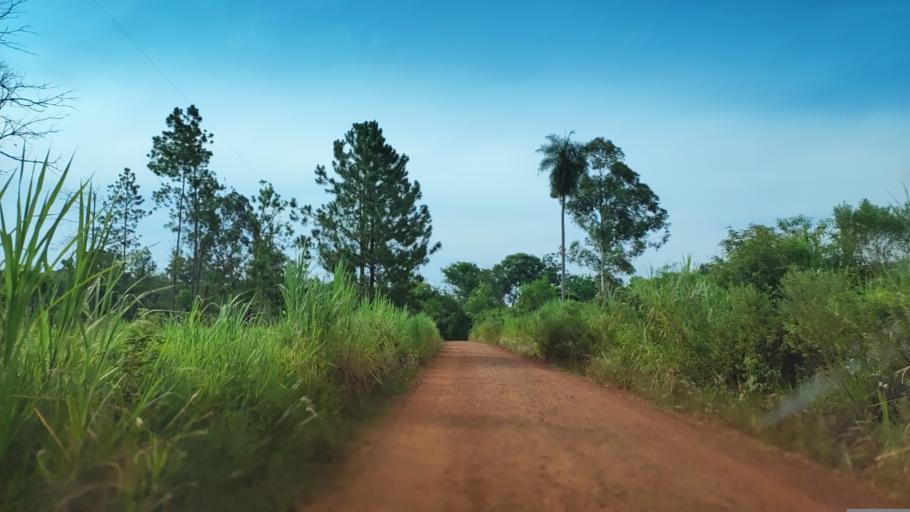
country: AR
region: Misiones
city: Gobernador Roca
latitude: -27.1776
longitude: -55.5009
